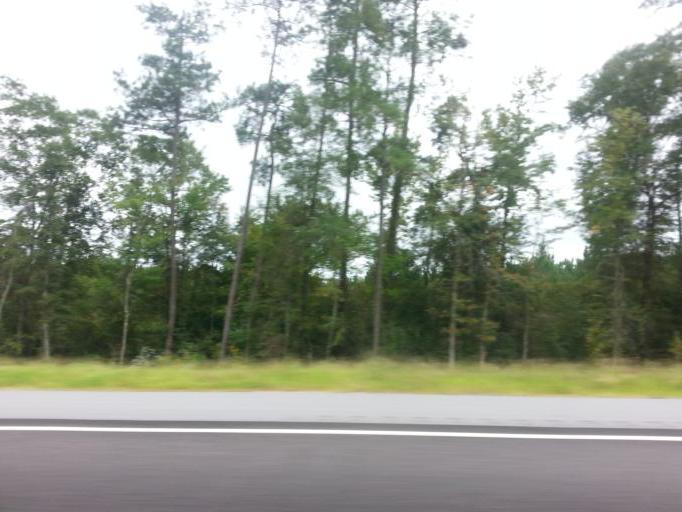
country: US
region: Alabama
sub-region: Conecuh County
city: Evergreen
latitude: 31.3560
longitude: -87.0718
